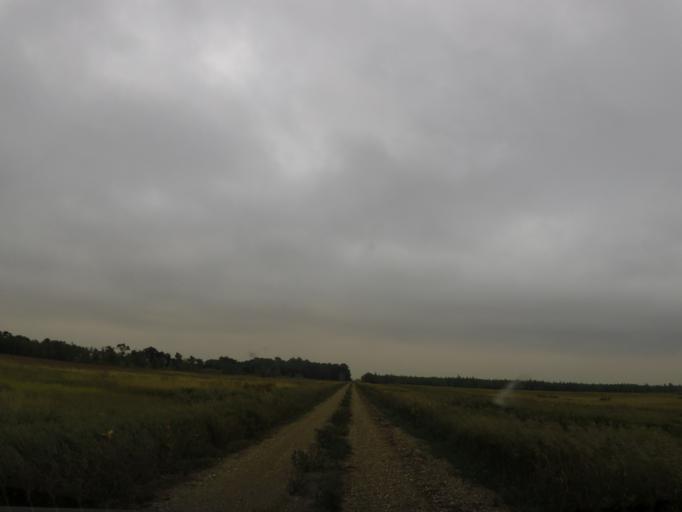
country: US
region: North Dakota
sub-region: Walsh County
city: Grafton
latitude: 48.4277
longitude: -97.1264
